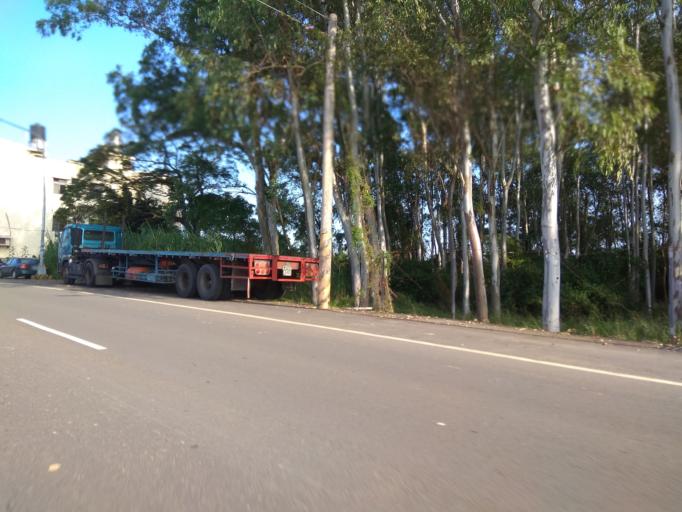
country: TW
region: Taiwan
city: Taoyuan City
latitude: 24.9667
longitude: 121.1406
